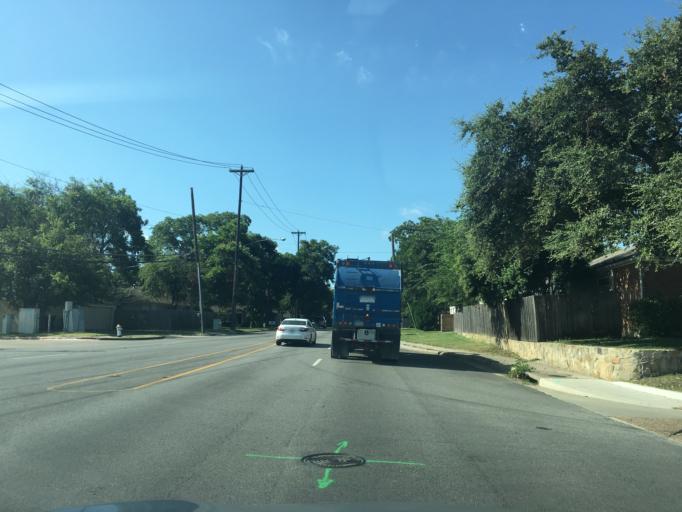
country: US
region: Texas
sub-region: Dallas County
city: Highland Park
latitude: 32.8357
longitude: -96.7531
